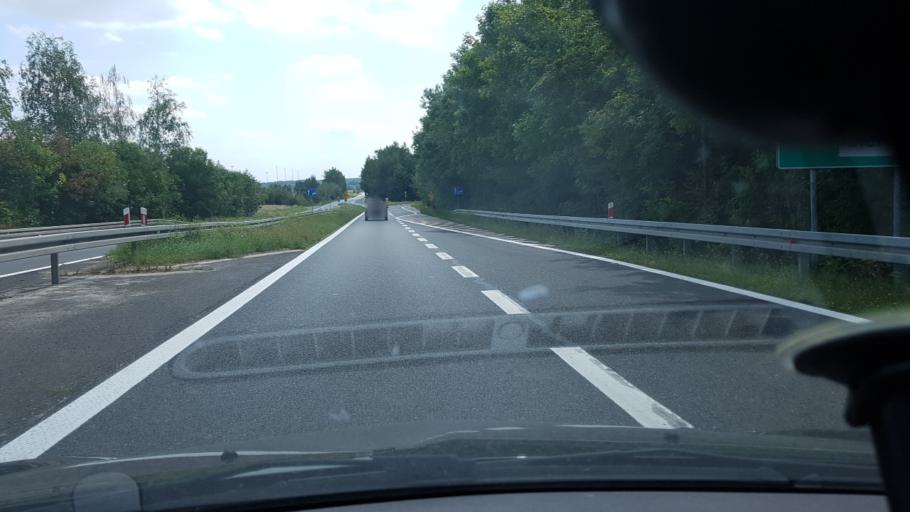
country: PL
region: Silesian Voivodeship
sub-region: Powiat bierunsko-ledzinski
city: Bierun
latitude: 50.1000
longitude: 19.0977
